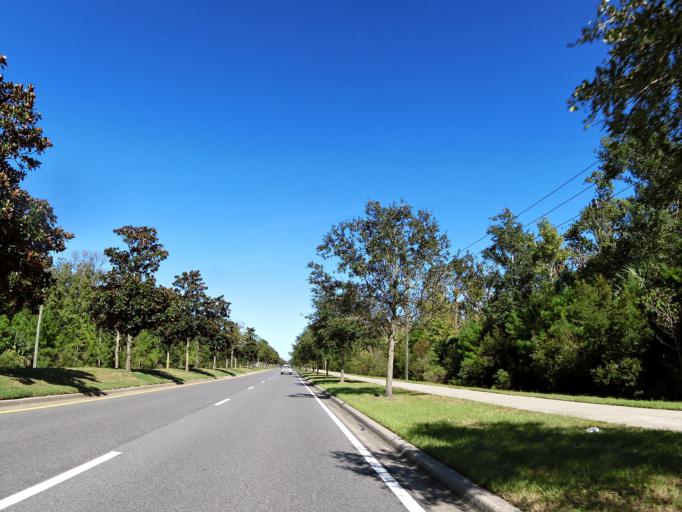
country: US
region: Florida
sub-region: Saint Johns County
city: Palm Valley
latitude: 30.1261
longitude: -81.3949
